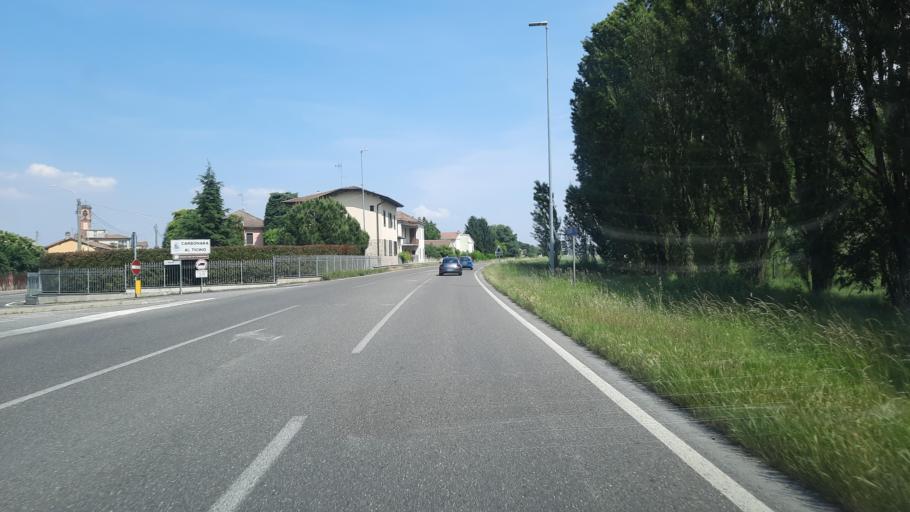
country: IT
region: Lombardy
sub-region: Provincia di Pavia
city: Carbonara al Ticino
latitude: 45.1642
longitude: 9.0556
